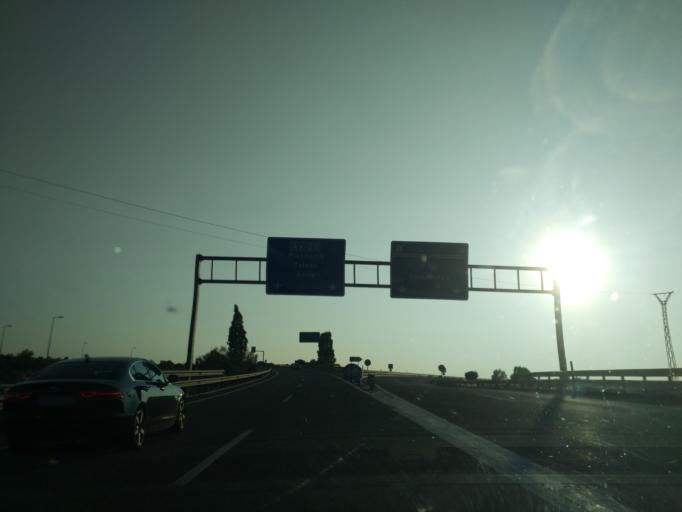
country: ES
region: Castille and Leon
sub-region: Provincia de Avila
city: Avila
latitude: 40.6695
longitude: -4.7134
